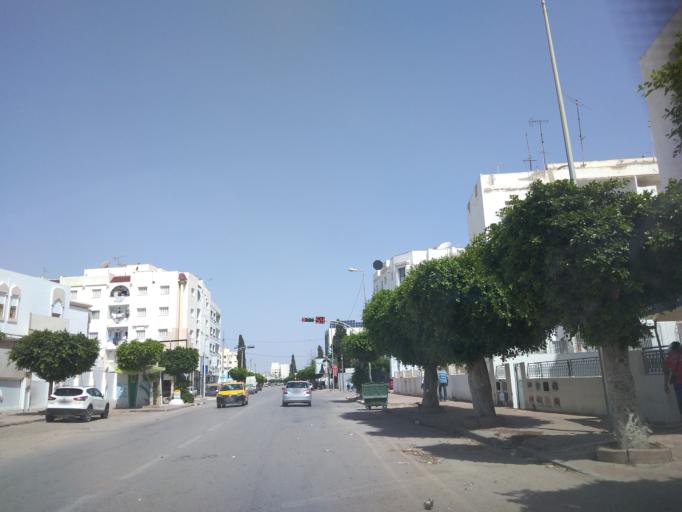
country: TN
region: Safaqis
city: Sfax
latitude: 34.7423
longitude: 10.7501
